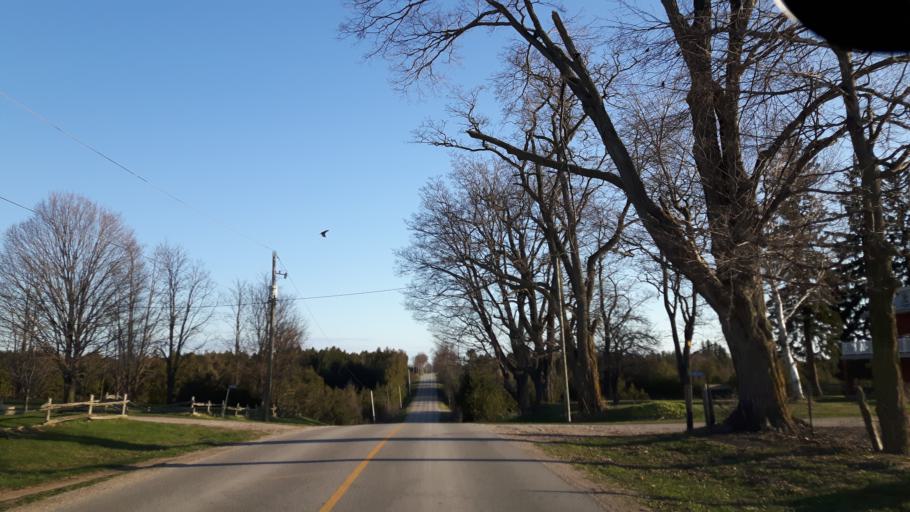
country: CA
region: Ontario
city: Goderich
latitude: 43.6698
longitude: -81.6847
